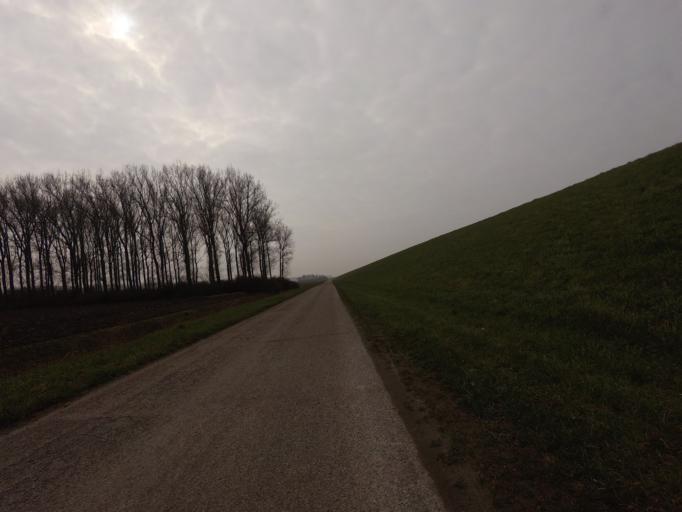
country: NL
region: North Brabant
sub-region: Gemeente Woensdrecht
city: Woensdrecht
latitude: 51.3453
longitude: 4.2074
